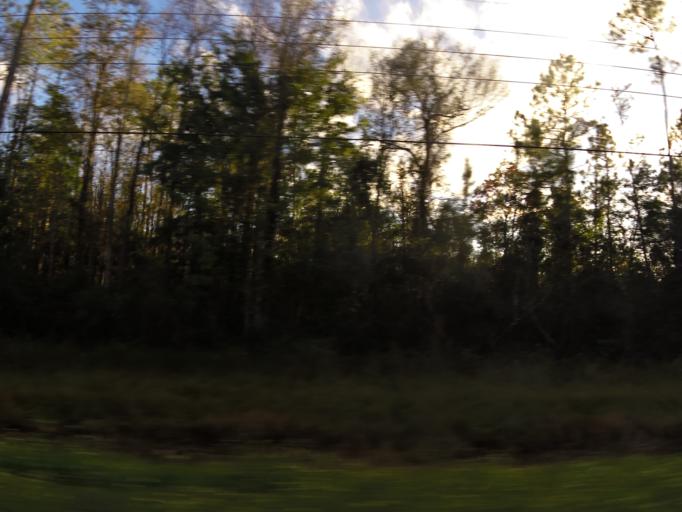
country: US
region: Florida
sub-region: Saint Johns County
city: Fruit Cove
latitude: 30.0502
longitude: -81.5878
